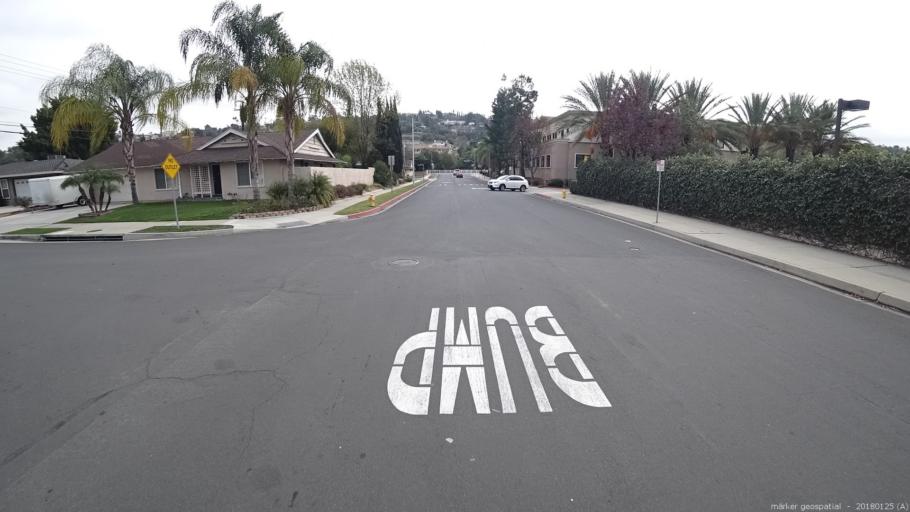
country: US
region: California
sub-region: Los Angeles County
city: Walnut
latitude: 33.9769
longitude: -117.8371
